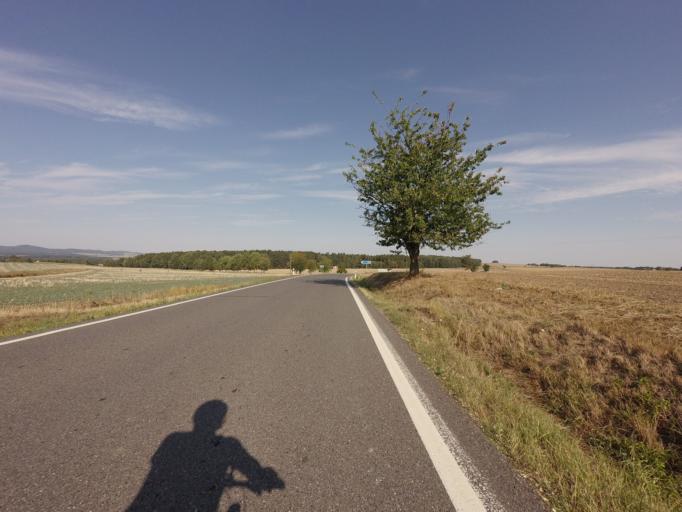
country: CZ
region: Jihocesky
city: Bernartice
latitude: 49.3100
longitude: 14.3751
